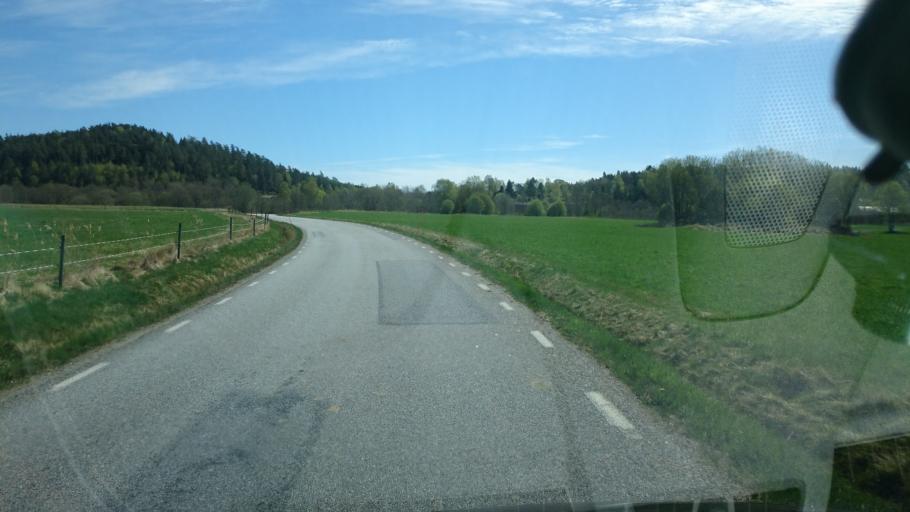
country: SE
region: Vaestra Goetaland
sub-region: Munkedals Kommun
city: Munkedal
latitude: 58.3763
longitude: 11.6795
